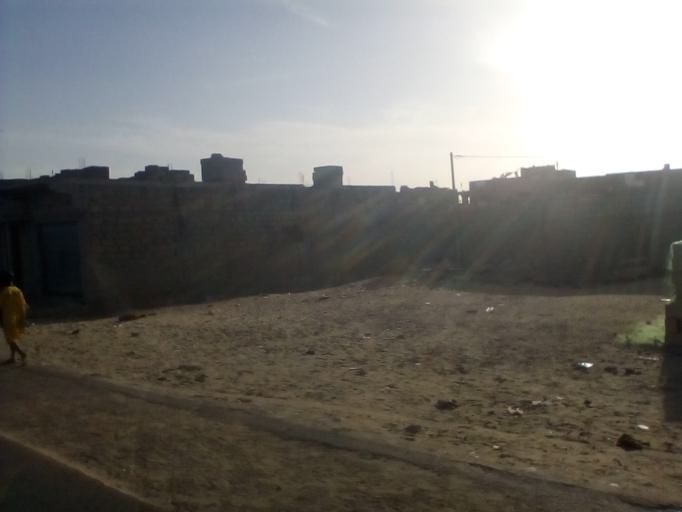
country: SN
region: Saint-Louis
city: Saint-Louis
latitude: 15.9975
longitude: -16.4836
